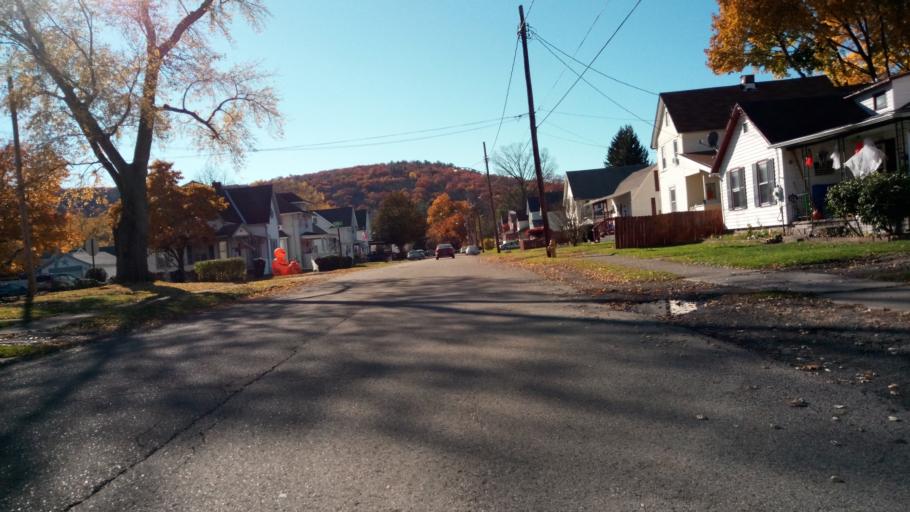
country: US
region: New York
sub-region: Chemung County
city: Southport
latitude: 42.0713
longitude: -76.8159
